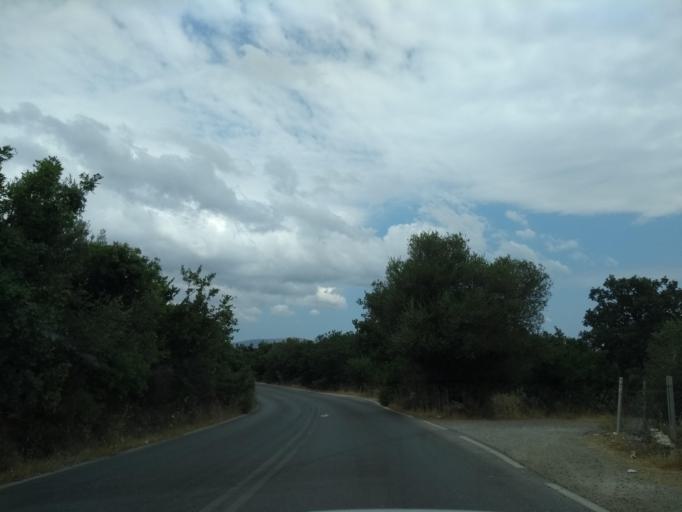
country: GR
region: Crete
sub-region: Nomos Chanias
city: Kalivai
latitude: 35.4086
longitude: 24.2092
